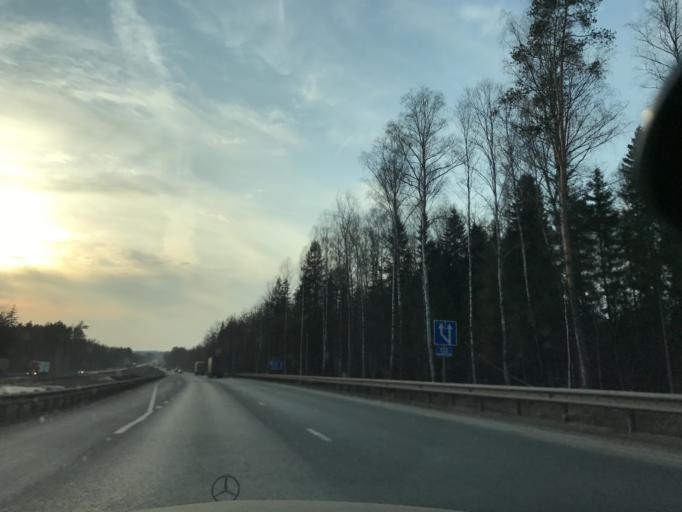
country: RU
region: Vladimir
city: Kosterevo
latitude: 55.9587
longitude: 39.6637
